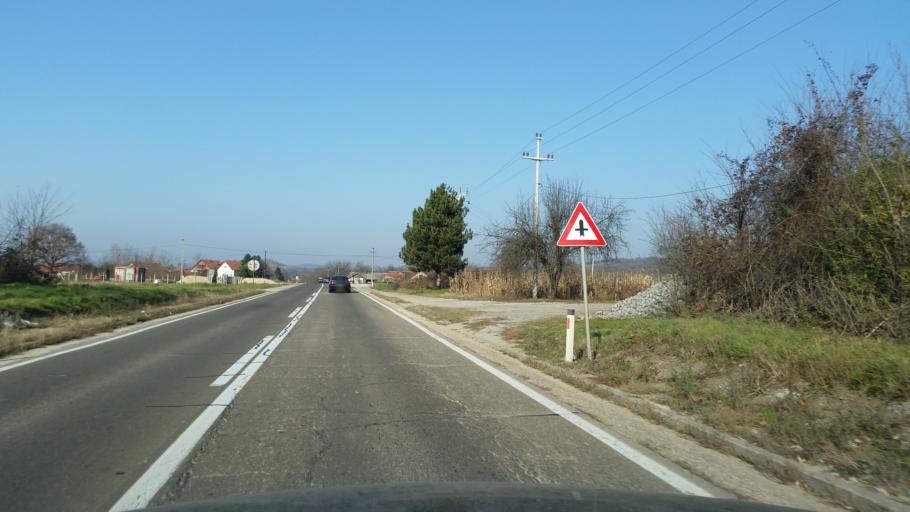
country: RS
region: Central Serbia
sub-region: Kolubarski Okrug
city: Ljig
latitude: 44.2693
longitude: 20.2843
